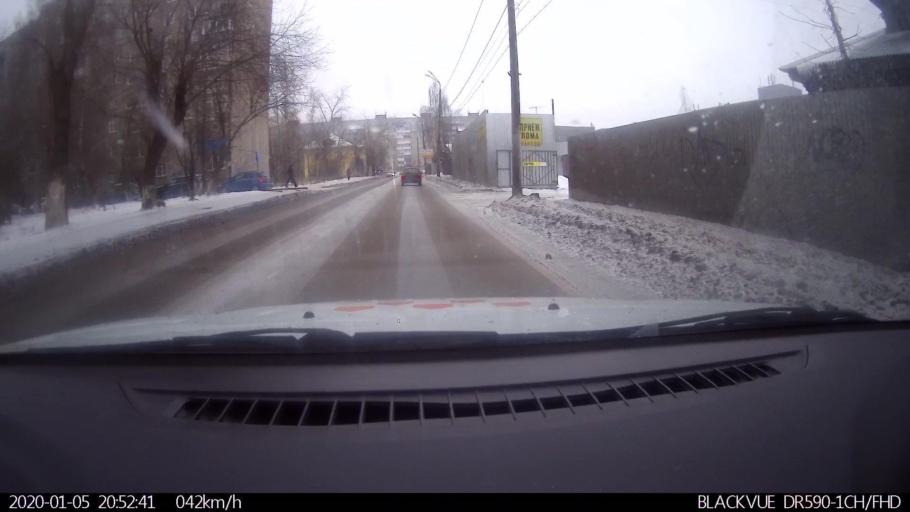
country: RU
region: Nizjnij Novgorod
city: Gorbatovka
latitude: 56.3661
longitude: 43.8173
